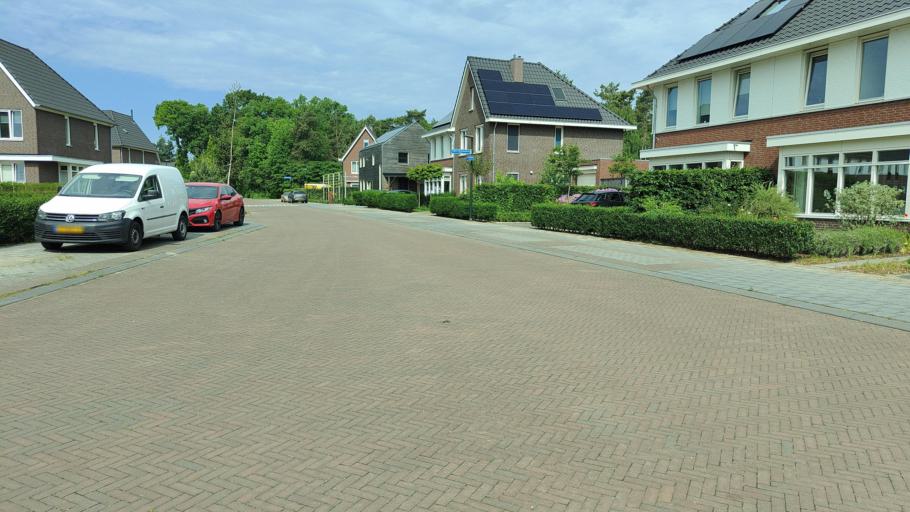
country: NL
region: Gelderland
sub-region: Gemeente Renkum
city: Wolfheze
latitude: 52.0059
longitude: 5.7978
